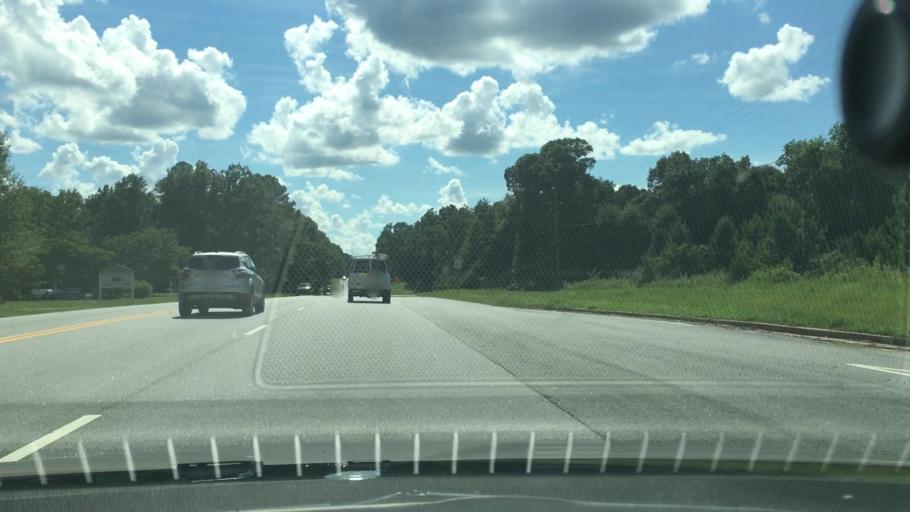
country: US
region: Georgia
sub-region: Butts County
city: Jackson
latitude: 33.2919
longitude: -83.9882
